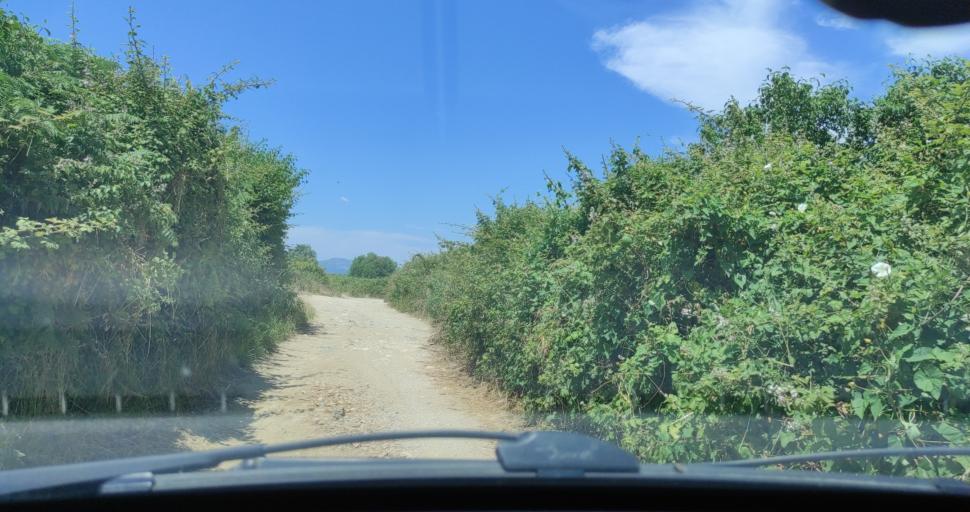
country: AL
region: Shkoder
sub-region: Rrethi i Shkodres
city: Velipoje
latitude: 41.8825
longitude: 19.3920
